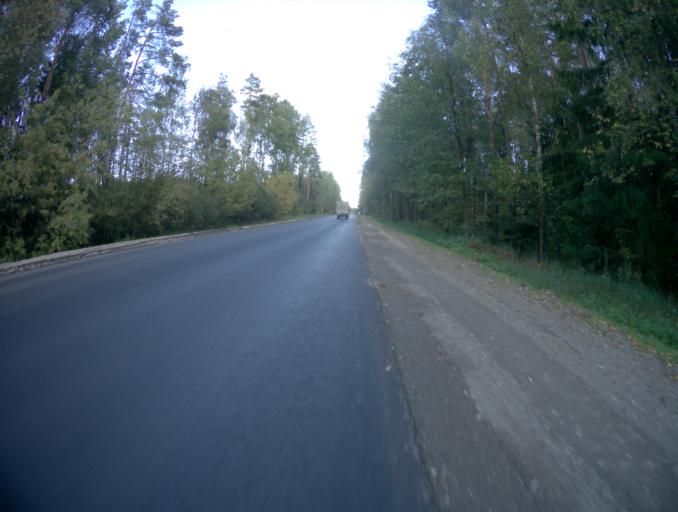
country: RU
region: Moskovskaya
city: Kerva
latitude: 55.5660
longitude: 39.6393
